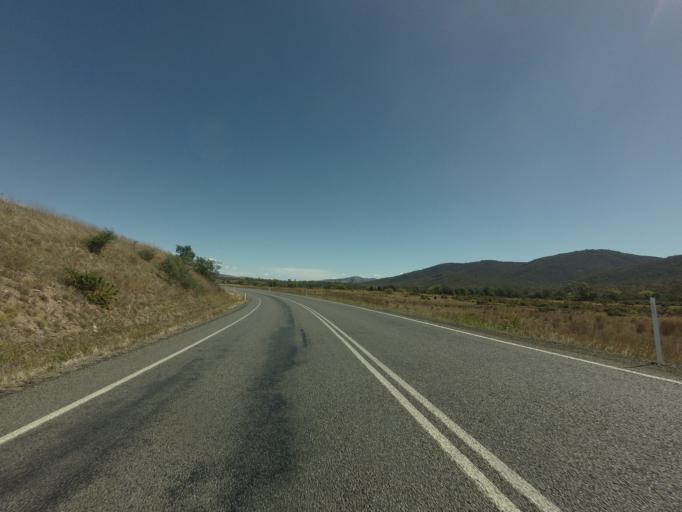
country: AU
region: Tasmania
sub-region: Northern Midlands
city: Evandale
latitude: -41.7453
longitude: 147.7848
